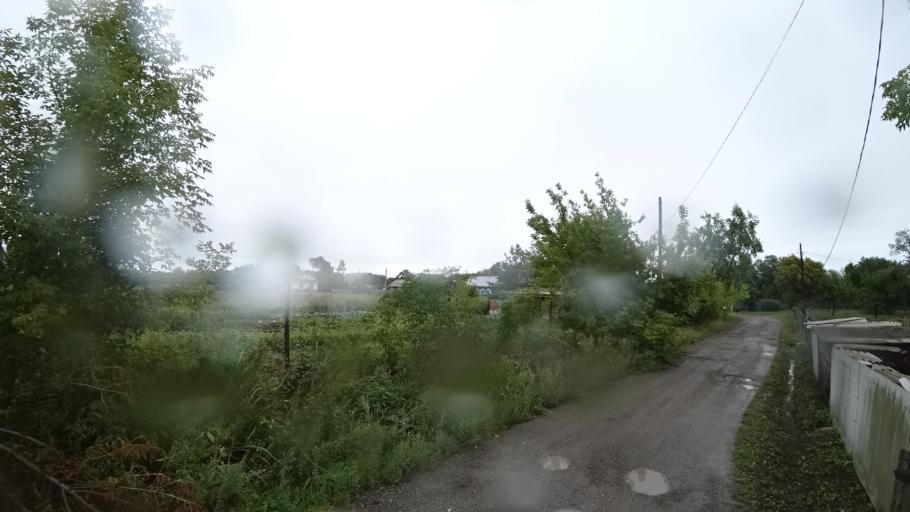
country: RU
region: Primorskiy
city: Monastyrishche
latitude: 44.2026
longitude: 132.4251
